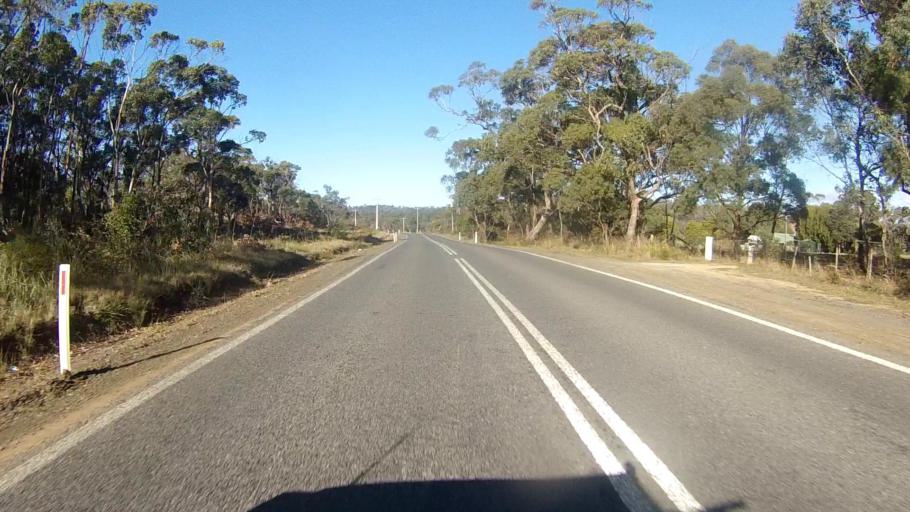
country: AU
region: Tasmania
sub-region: Sorell
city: Sorell
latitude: -42.9380
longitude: 147.8605
